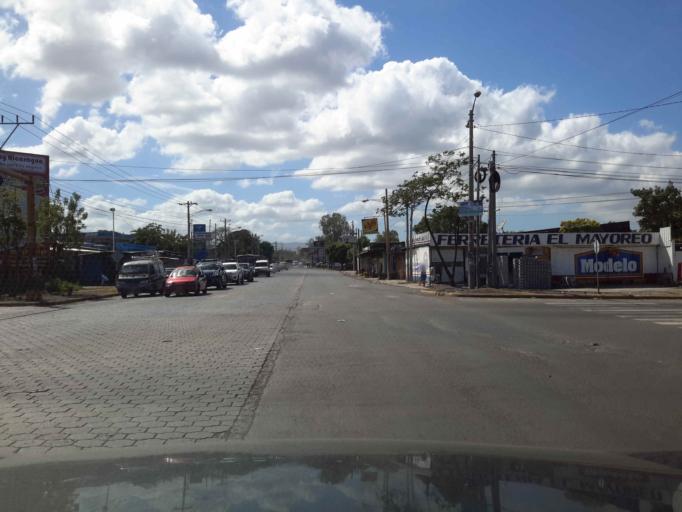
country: NI
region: Managua
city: Managua
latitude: 12.1347
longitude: -86.1986
